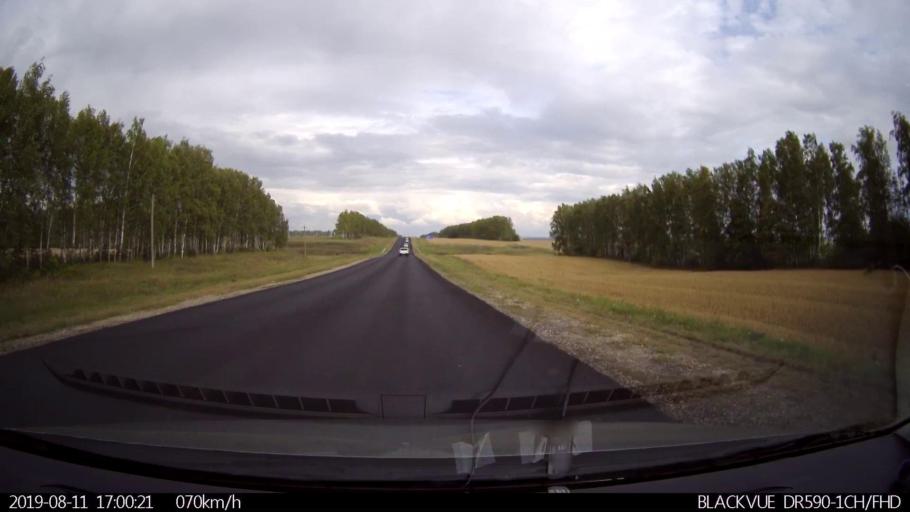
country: RU
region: Ulyanovsk
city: Mayna
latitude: 54.3105
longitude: 47.6778
